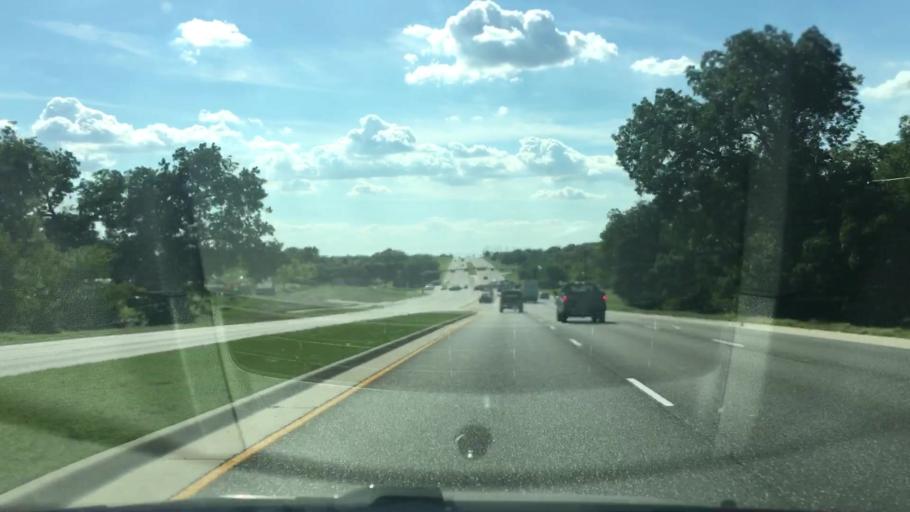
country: US
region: Texas
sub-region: Collin County
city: Prosper
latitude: 33.2191
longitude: -96.7190
